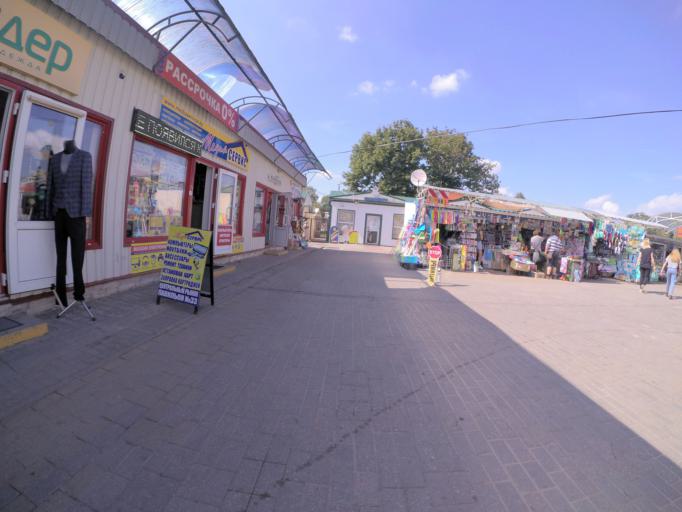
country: BY
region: Grodnenskaya
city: Hrodna
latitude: 53.6726
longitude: 23.8384
